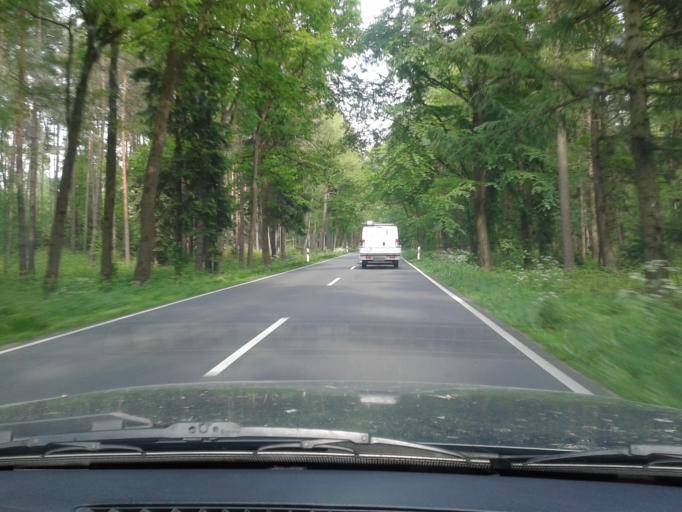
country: DE
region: Lower Saxony
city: Wienhausen
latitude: 52.6240
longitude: 10.1461
